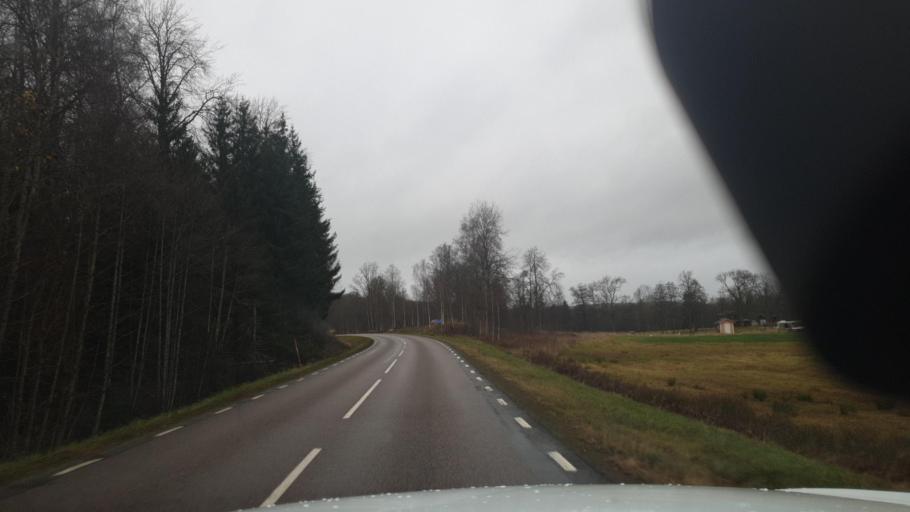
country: SE
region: Vaermland
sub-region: Arvika Kommun
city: Arvika
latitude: 59.4846
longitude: 12.6964
